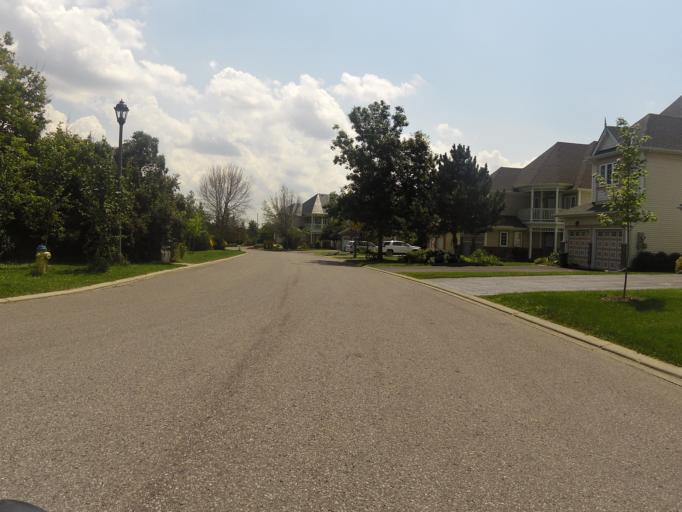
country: CA
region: Ontario
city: Bells Corners
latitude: 45.3125
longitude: -75.9303
